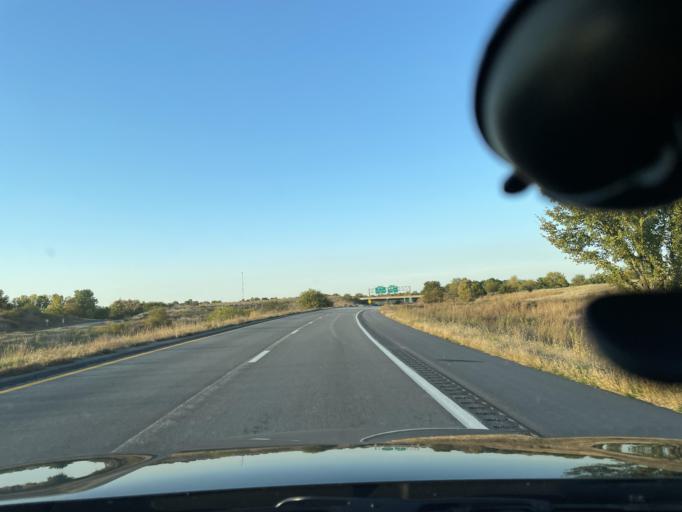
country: US
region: Missouri
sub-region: Andrew County
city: Country Club Village
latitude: 39.8810
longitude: -94.8571
